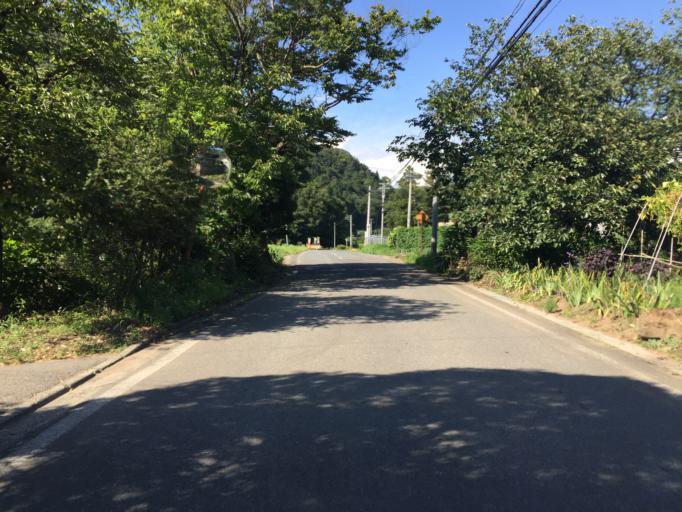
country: JP
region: Fukushima
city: Hobaramachi
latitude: 37.7495
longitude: 140.5661
